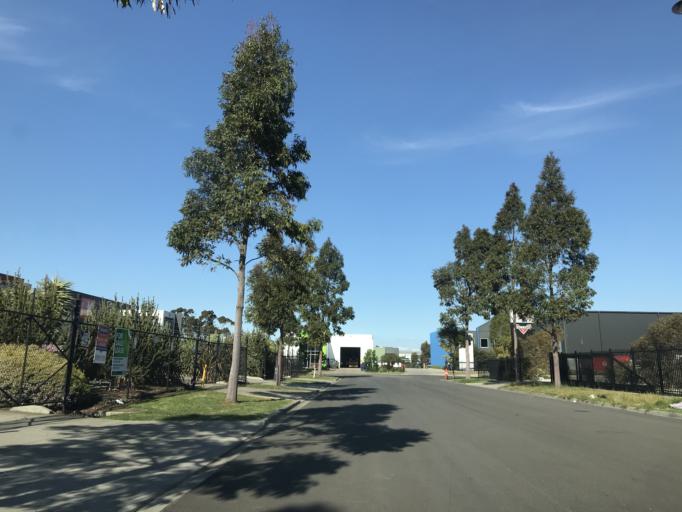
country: AU
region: Victoria
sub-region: Wyndham
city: Truganina
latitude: -37.8049
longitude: 144.7577
